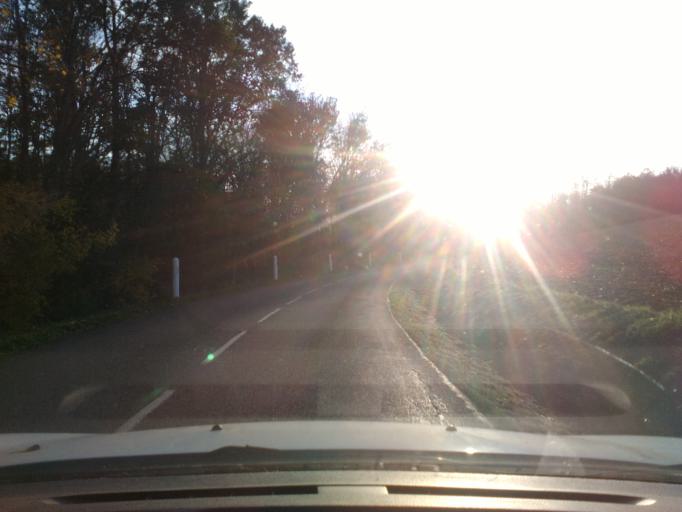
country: FR
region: Lorraine
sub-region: Departement des Vosges
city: Mirecourt
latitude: 48.2156
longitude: 6.1548
